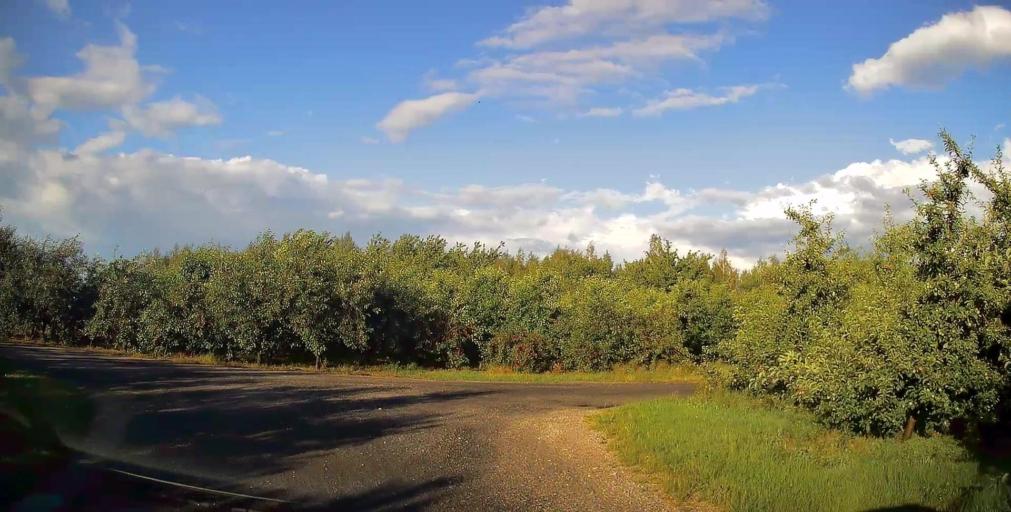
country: PL
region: Masovian Voivodeship
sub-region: Powiat grojecki
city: Goszczyn
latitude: 51.7459
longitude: 20.8871
